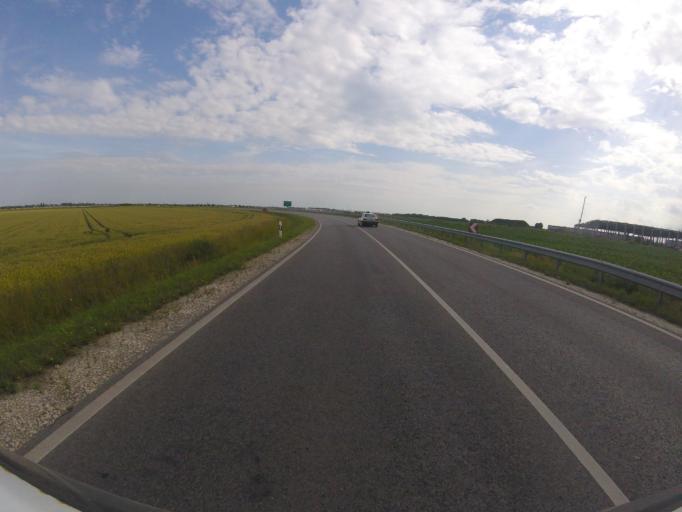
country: HU
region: Pest
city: Szigetszentmiklos
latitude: 47.3740
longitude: 19.0299
